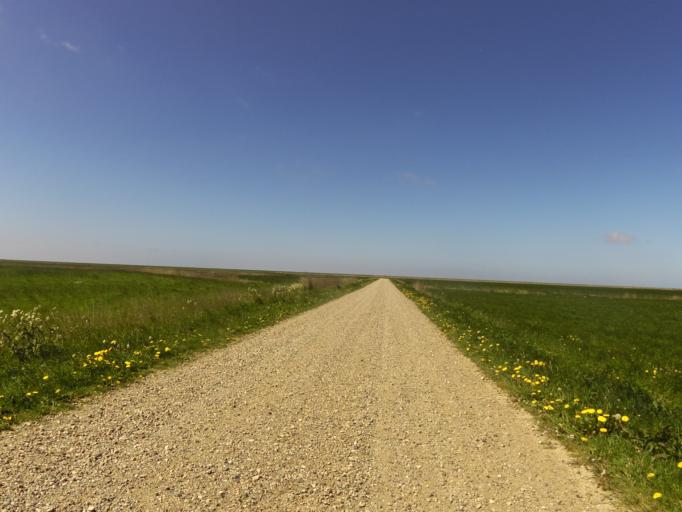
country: DK
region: South Denmark
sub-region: Tonder Kommune
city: Sherrebek
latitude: 55.2383
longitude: 8.6926
